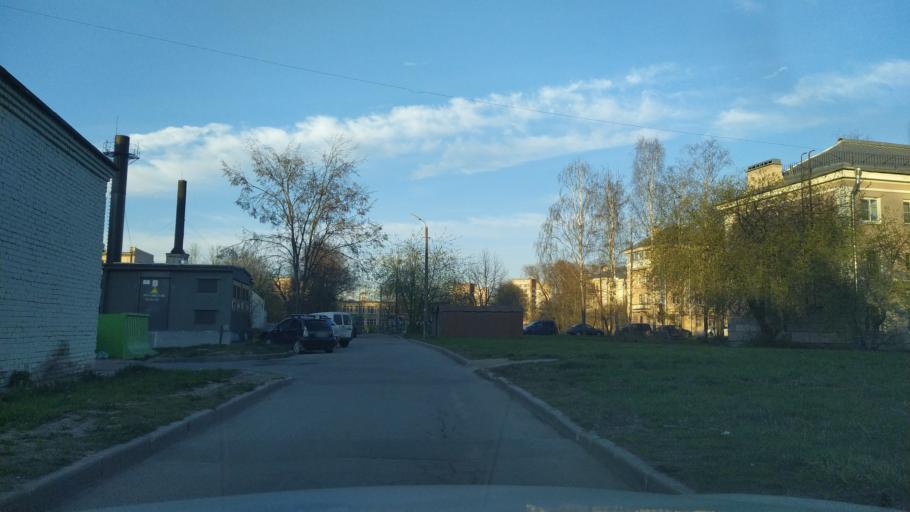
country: RU
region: St.-Petersburg
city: Pushkin
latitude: 59.7051
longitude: 30.3661
